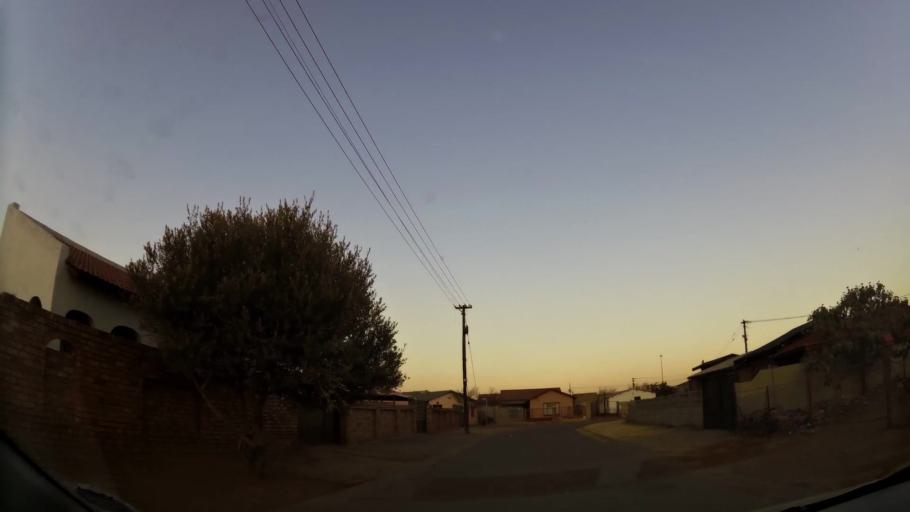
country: ZA
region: Gauteng
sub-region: West Rand District Municipality
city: Randfontein
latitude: -26.2020
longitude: 27.7132
